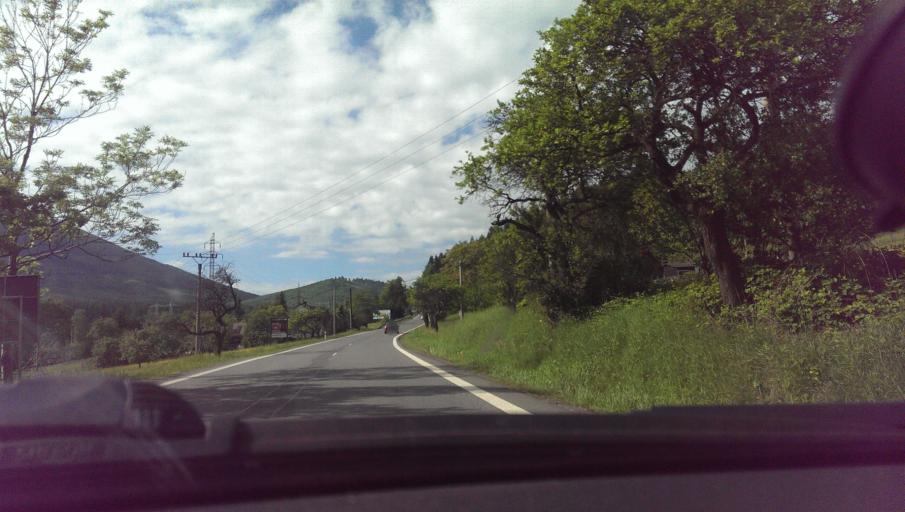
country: CZ
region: Moravskoslezsky
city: Frenstat pod Radhostem
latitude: 49.5136
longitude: 18.1965
